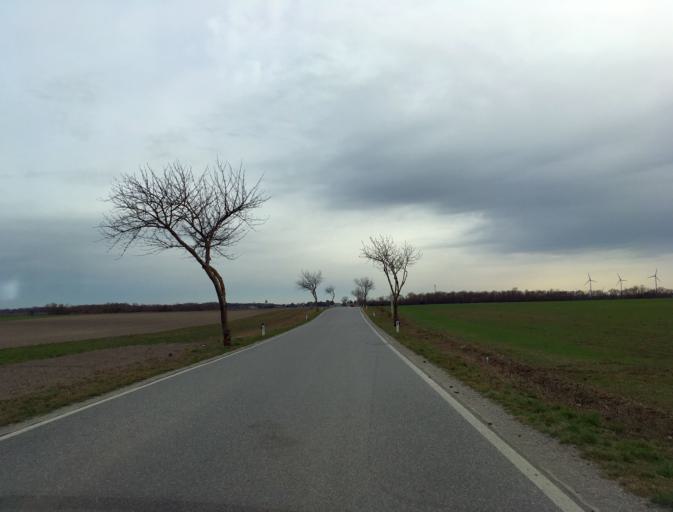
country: AT
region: Lower Austria
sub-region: Politischer Bezirk Ganserndorf
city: Leopoldsdorf im Marchfelde
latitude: 48.2377
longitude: 16.6716
